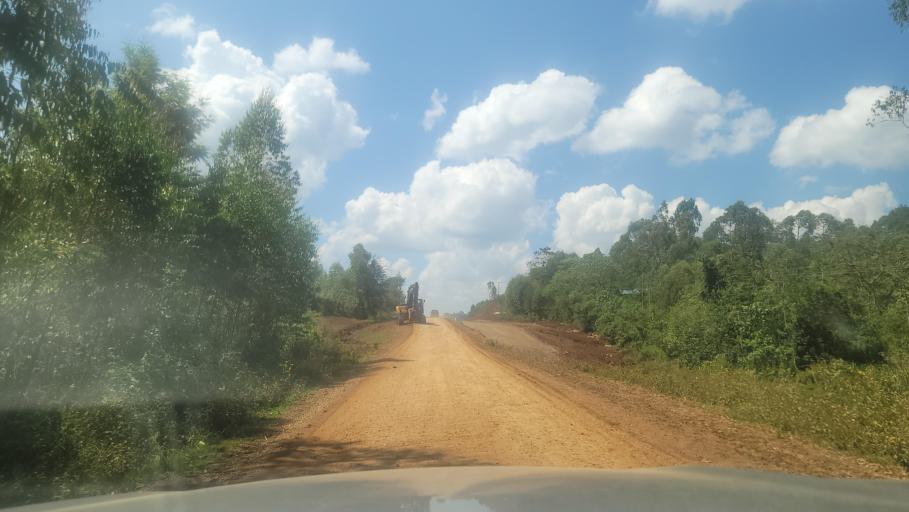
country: ET
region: Oromiya
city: Agaro
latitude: 7.7660
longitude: 36.3001
